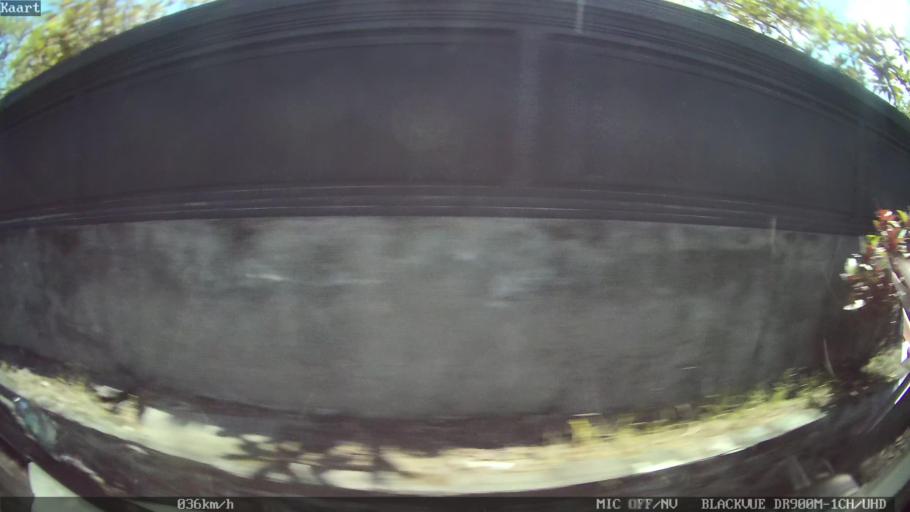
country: ID
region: Bali
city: Banjar Kelodan
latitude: -8.5504
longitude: 115.3352
